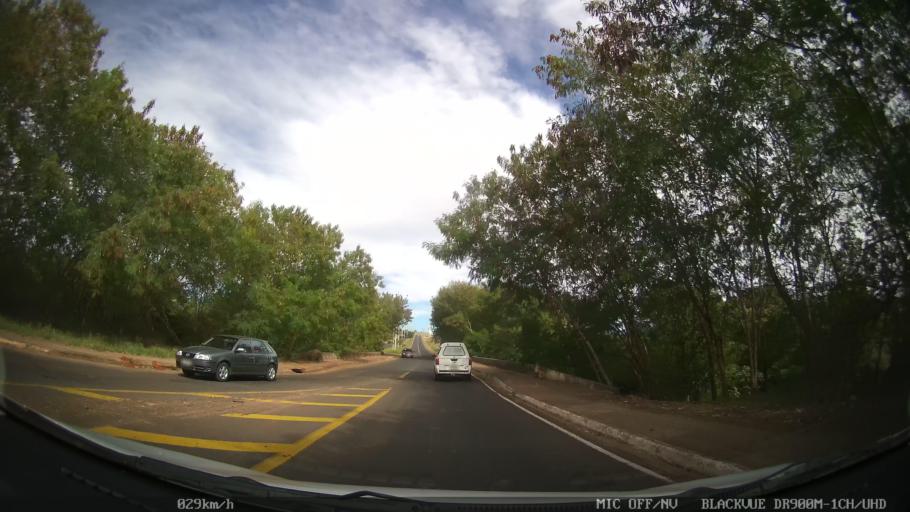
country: BR
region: Sao Paulo
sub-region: Catanduva
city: Catanduva
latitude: -21.1500
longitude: -48.9508
